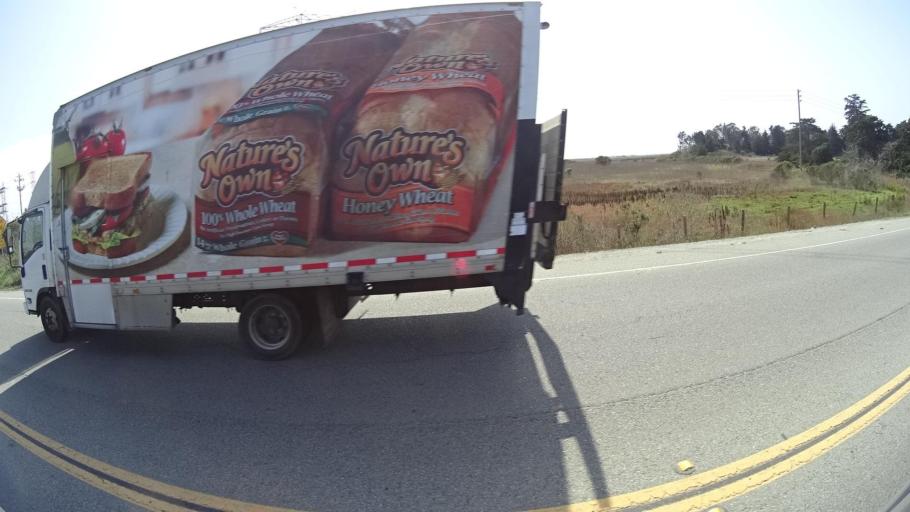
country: US
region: California
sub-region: Monterey County
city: Castroville
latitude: 36.8010
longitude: -121.7702
